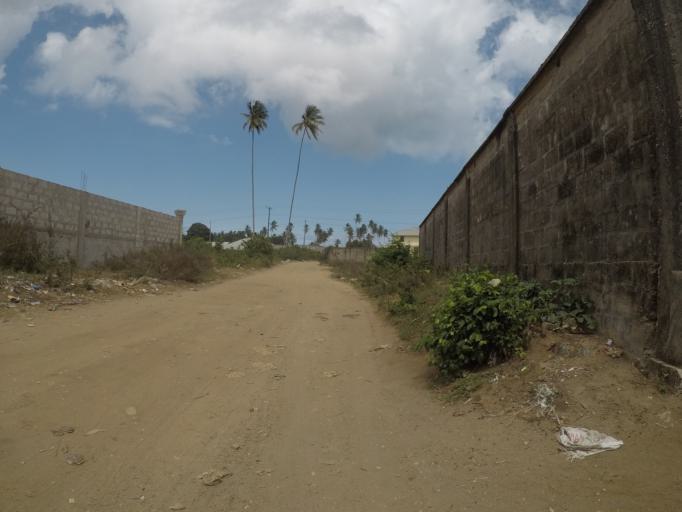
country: TZ
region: Zanzibar Urban/West
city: Zanzibar
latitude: -6.2061
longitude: 39.2281
